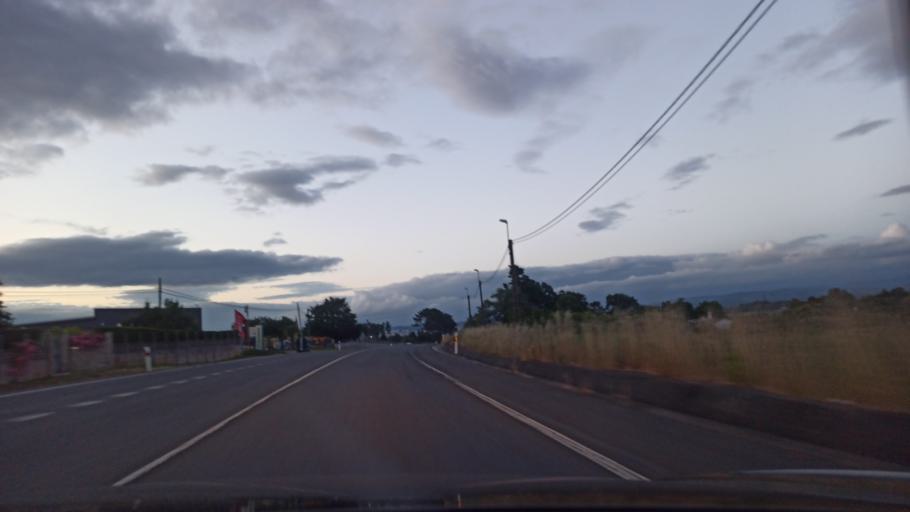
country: ES
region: Galicia
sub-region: Provincia de Lugo
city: Lugo
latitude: 42.9658
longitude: -7.5987
